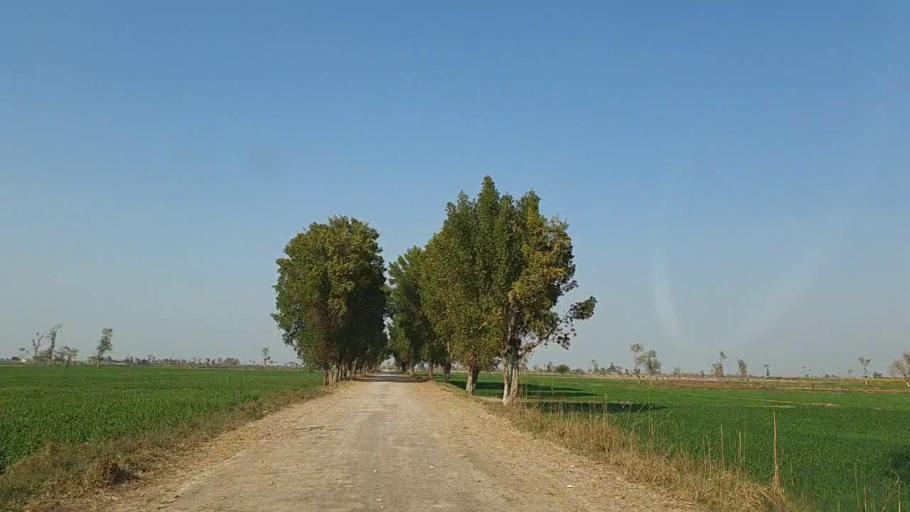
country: PK
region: Sindh
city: Daur
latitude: 26.4836
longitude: 68.2973
